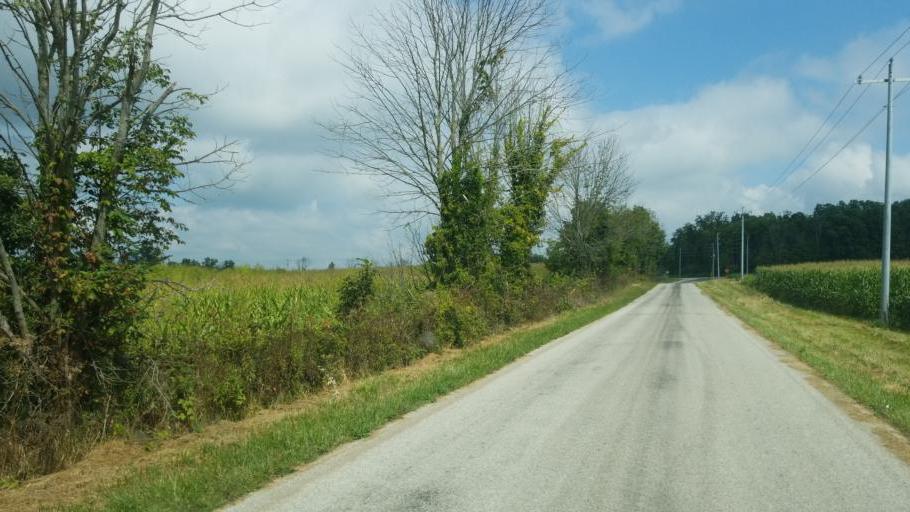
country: US
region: Ohio
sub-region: Licking County
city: Utica
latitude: 40.2292
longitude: -82.4834
